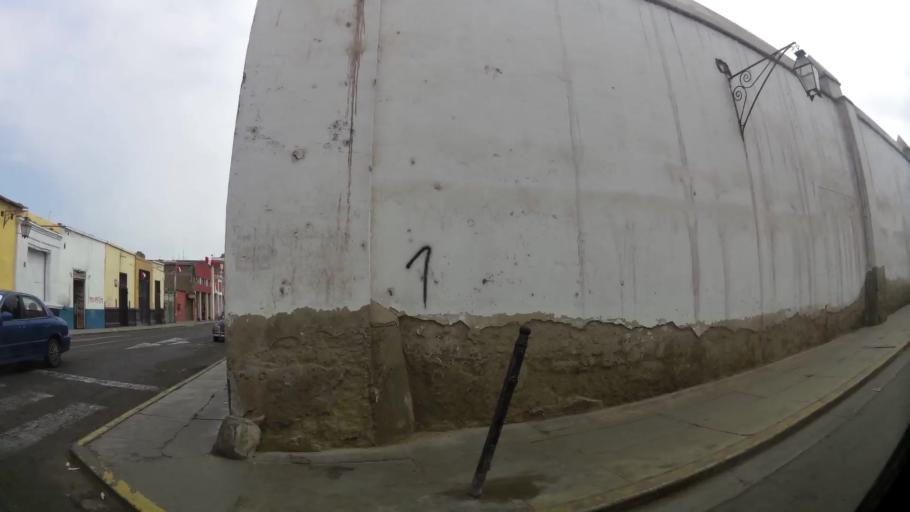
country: PE
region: La Libertad
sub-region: Provincia de Trujillo
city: Trujillo
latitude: -8.1090
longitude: -79.0225
